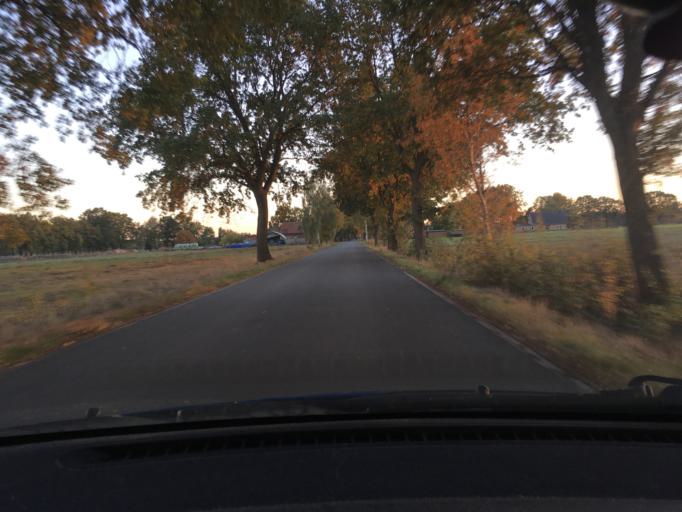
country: DE
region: Lower Saxony
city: Ludersburg
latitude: 53.3103
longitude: 10.6163
